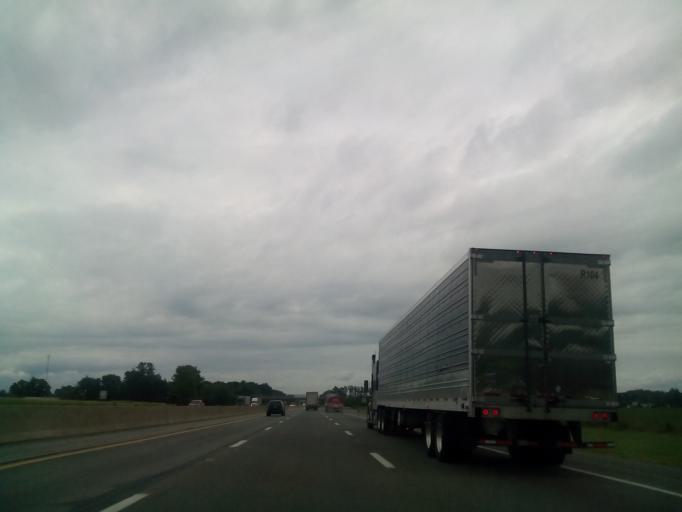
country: US
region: Ohio
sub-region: Huron County
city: Wakeman
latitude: 41.3327
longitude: -82.4225
